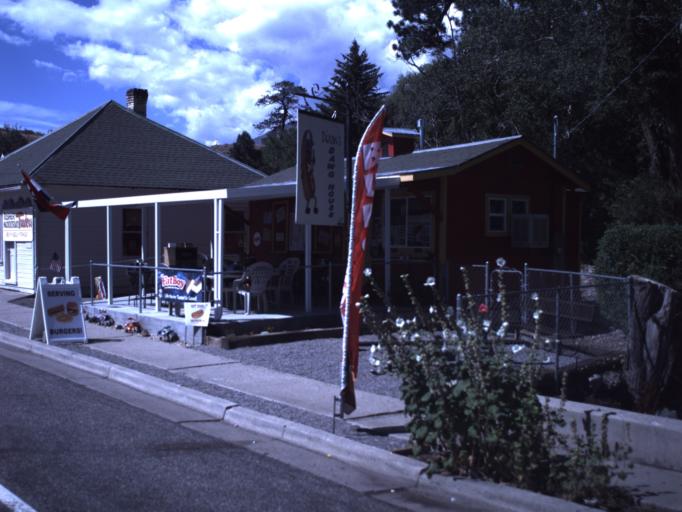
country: US
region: Utah
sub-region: Piute County
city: Junction
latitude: 38.4483
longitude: -112.2303
